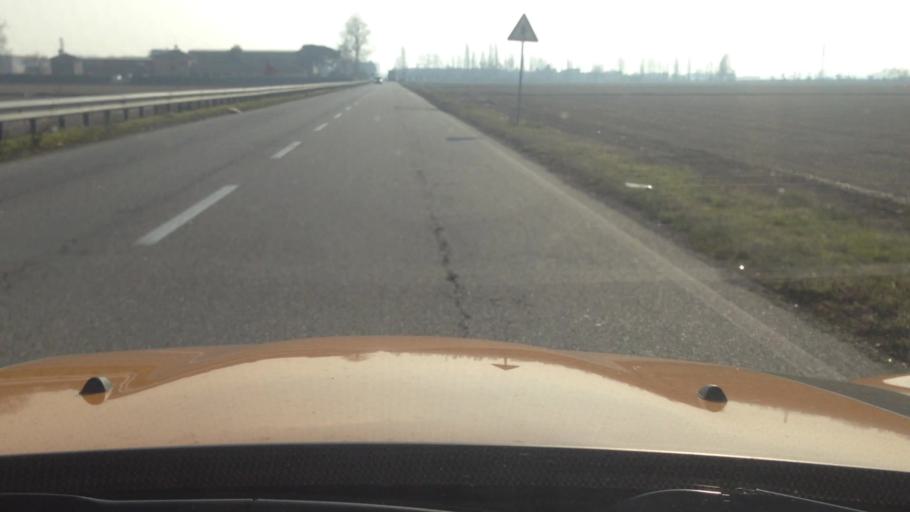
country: IT
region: Piedmont
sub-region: Provincia di Novara
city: San Pietro Mosezzo
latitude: 45.4663
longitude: 8.5579
